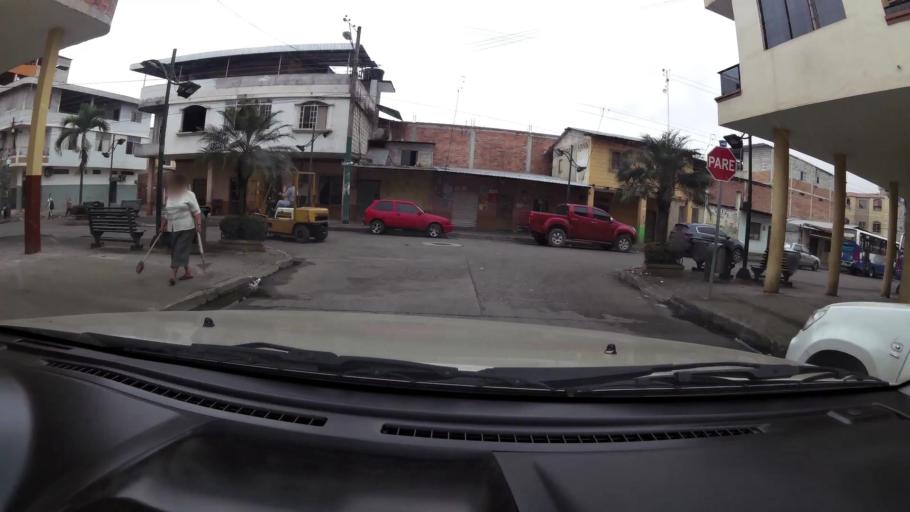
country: EC
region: El Oro
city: Pasaje
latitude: -3.3254
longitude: -79.8121
